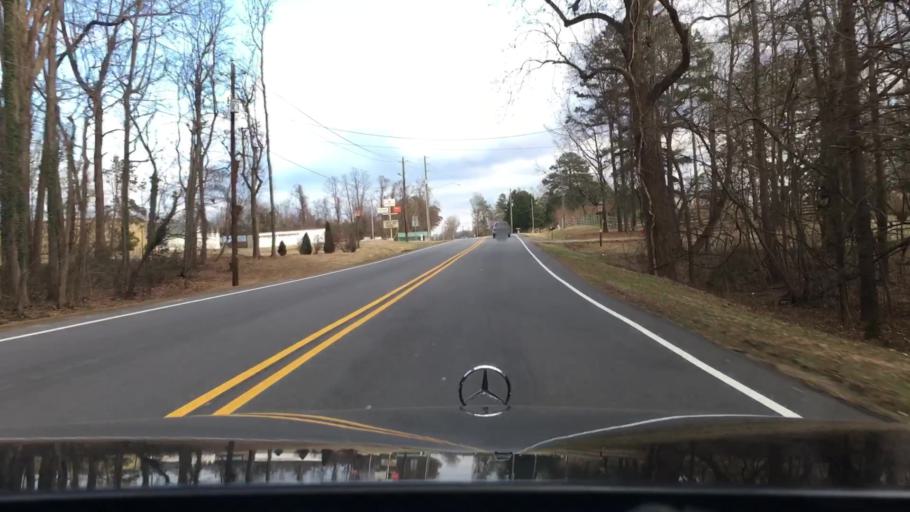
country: US
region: North Carolina
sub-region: Caswell County
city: Yanceyville
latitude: 36.4067
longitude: -79.3163
